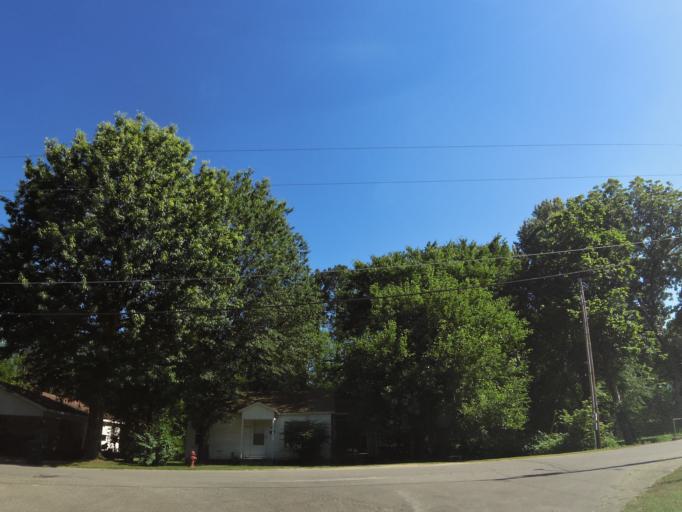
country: US
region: Arkansas
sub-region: Clay County
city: Piggott
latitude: 36.3819
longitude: -90.1954
